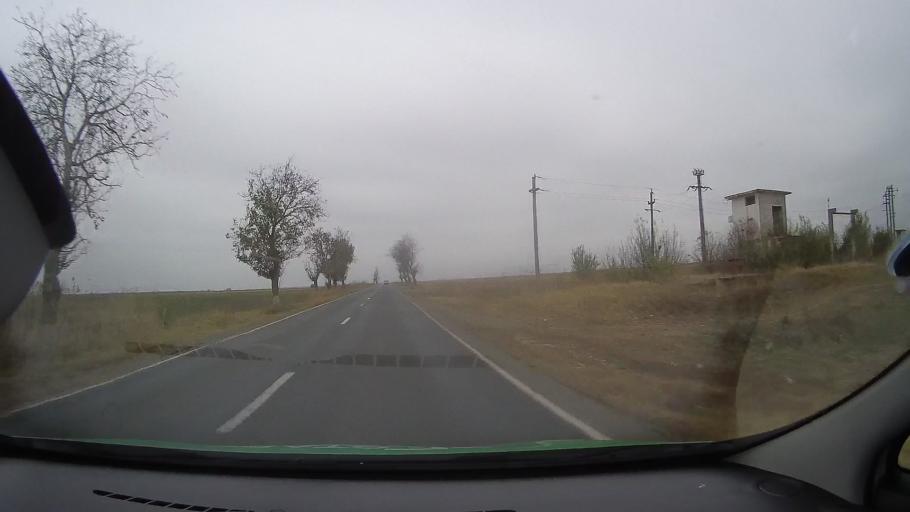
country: RO
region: Ialomita
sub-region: Comuna Scanteia
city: Scanteia
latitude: 44.7663
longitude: 27.4681
